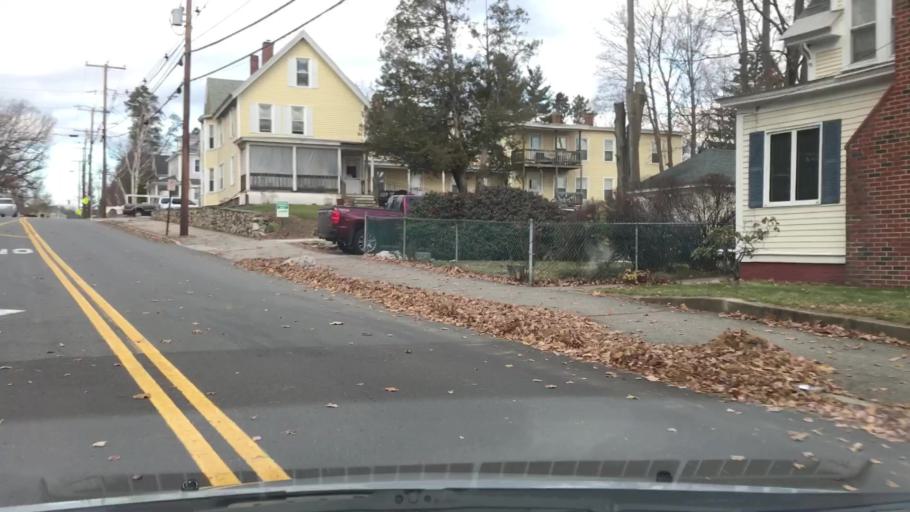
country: US
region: New Hampshire
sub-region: Hillsborough County
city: Manchester
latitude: 42.9829
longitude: -71.4347
